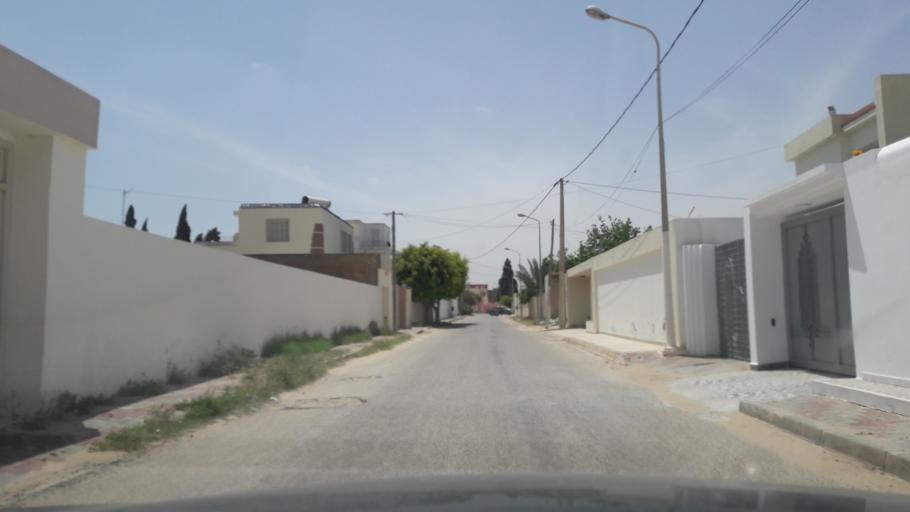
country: TN
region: Safaqis
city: Sfax
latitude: 34.7775
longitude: 10.7548
